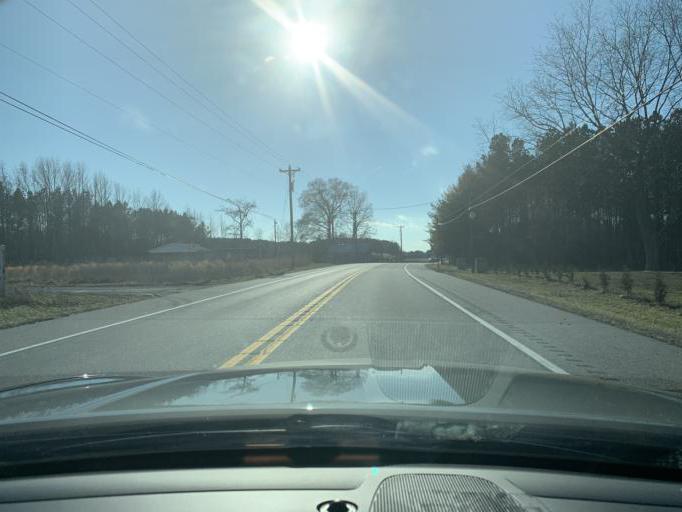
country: US
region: Maryland
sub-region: Queen Anne's County
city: Centreville
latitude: 39.1188
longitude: -76.0169
